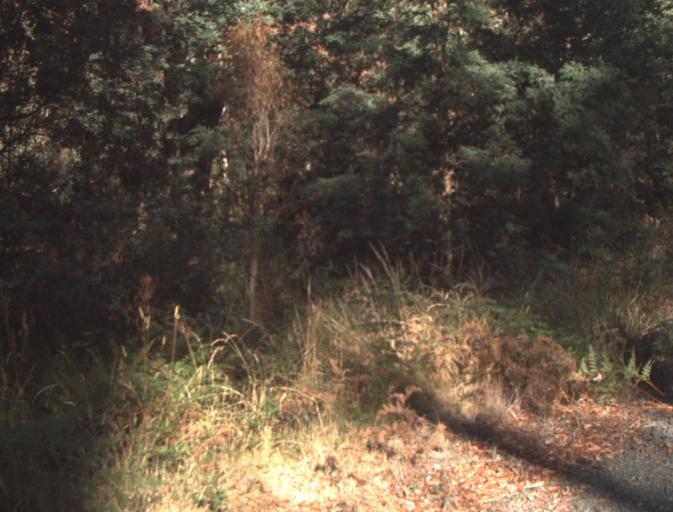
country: AU
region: Tasmania
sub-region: Launceston
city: Newstead
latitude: -41.3627
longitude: 147.3033
